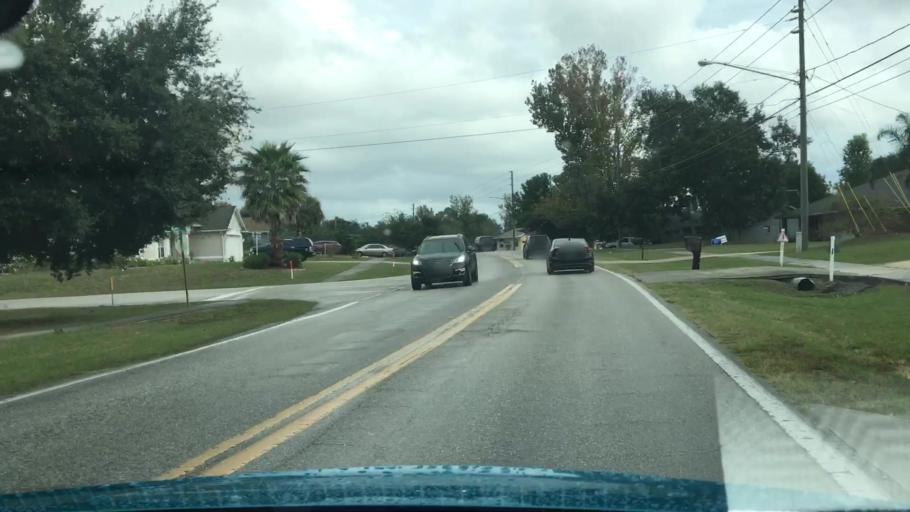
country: US
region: Florida
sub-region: Volusia County
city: Deltona
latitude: 28.9095
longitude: -81.2223
